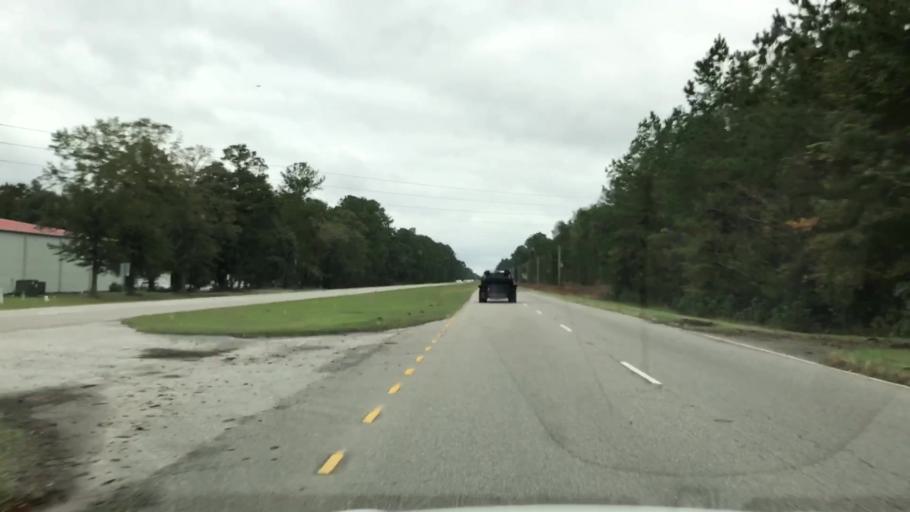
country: US
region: South Carolina
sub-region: Georgetown County
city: Georgetown
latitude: 33.3039
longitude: -79.3378
